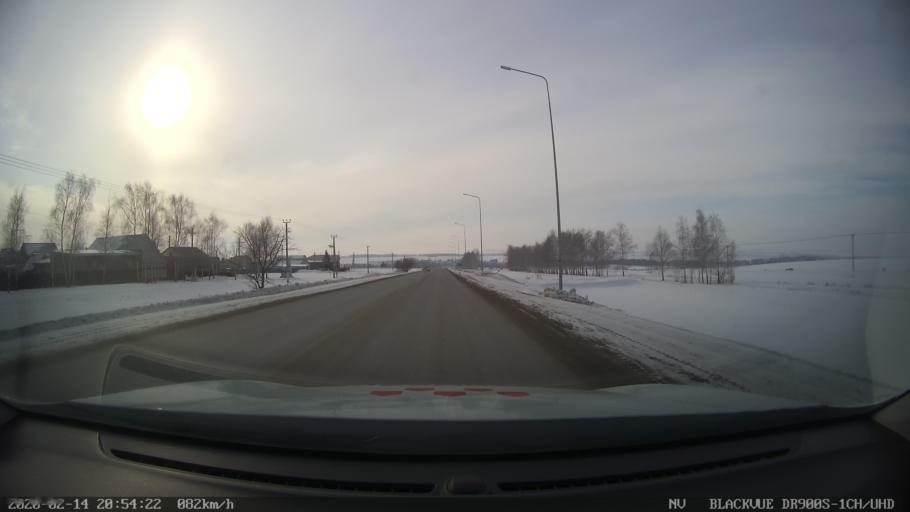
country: RU
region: Tatarstan
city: Kuybyshevskiy Zaton
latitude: 55.1866
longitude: 49.2434
